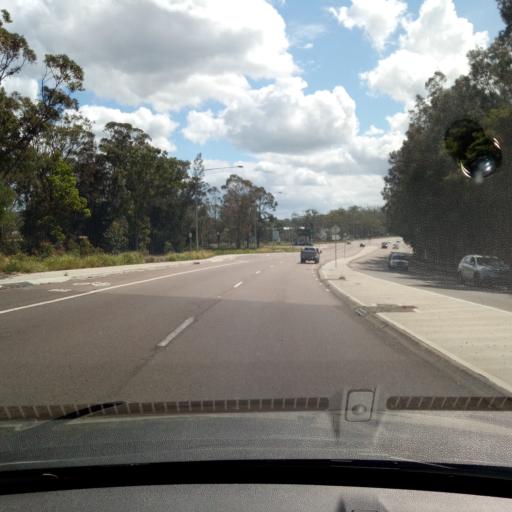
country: AU
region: New South Wales
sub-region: Wyong Shire
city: Chittaway Bay
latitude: -33.3301
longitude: 151.4293
